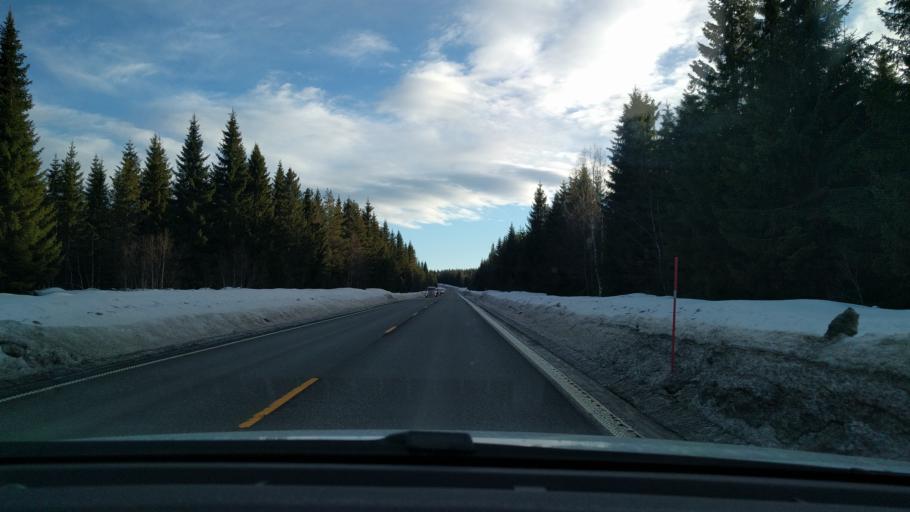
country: NO
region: Hedmark
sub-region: Trysil
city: Innbygda
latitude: 61.0781
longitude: 11.9774
